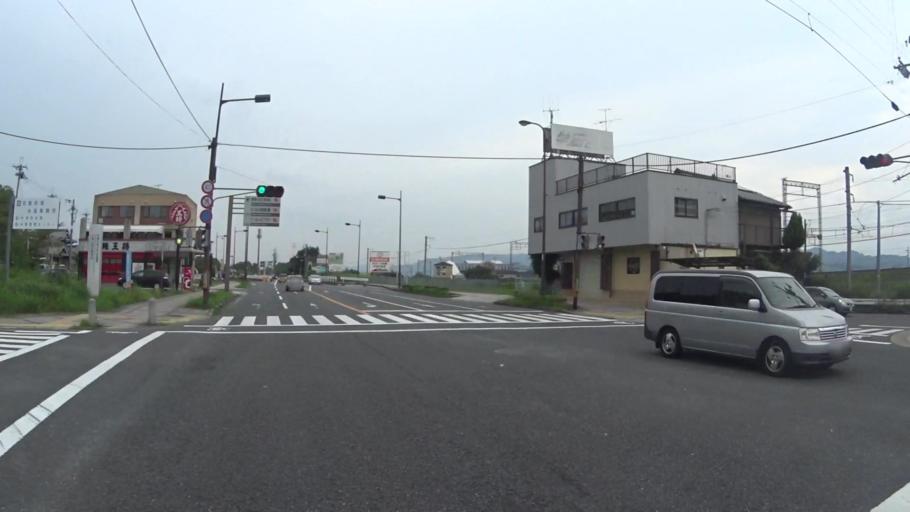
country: JP
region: Nara
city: Nara-shi
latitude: 34.7438
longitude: 135.7946
